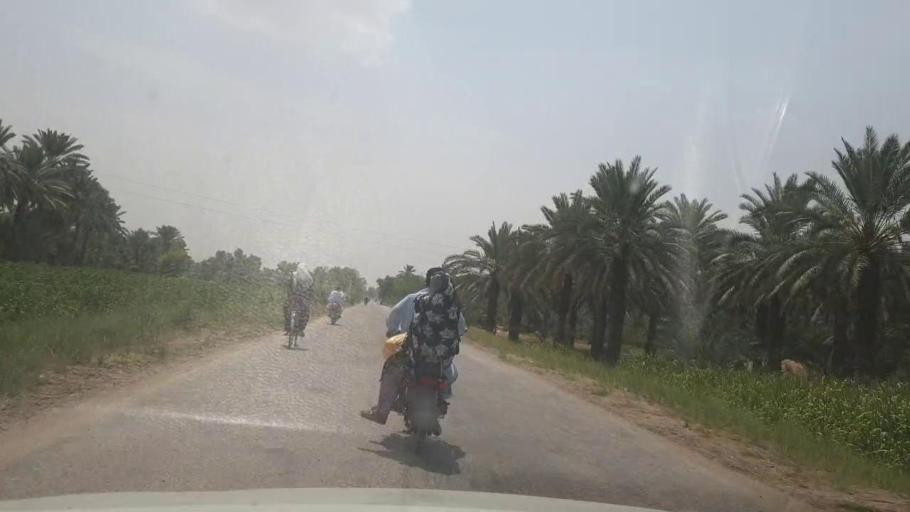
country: PK
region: Sindh
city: Kot Diji
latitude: 27.3718
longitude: 68.7208
